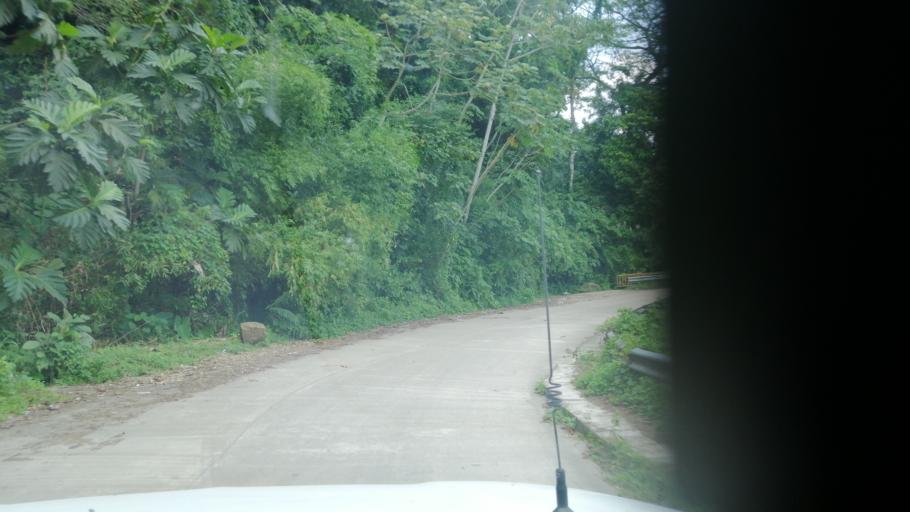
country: MX
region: Chiapas
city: Ostuacan
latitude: 17.3996
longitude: -93.3329
